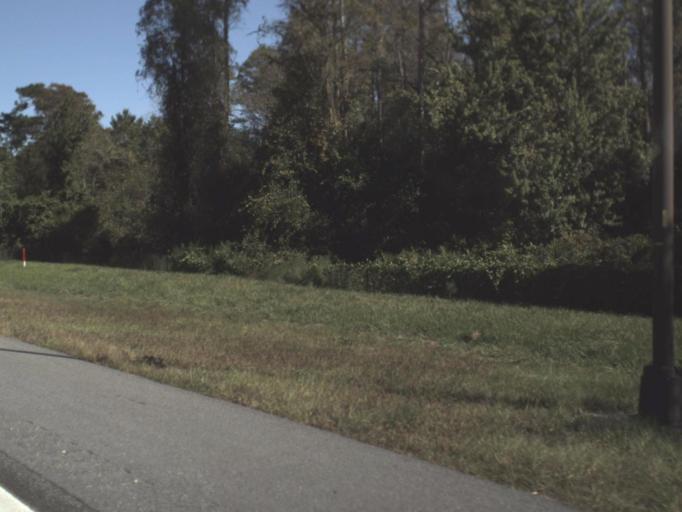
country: US
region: Florida
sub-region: Pasco County
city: Shady Hills
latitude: 28.3240
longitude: -82.5530
